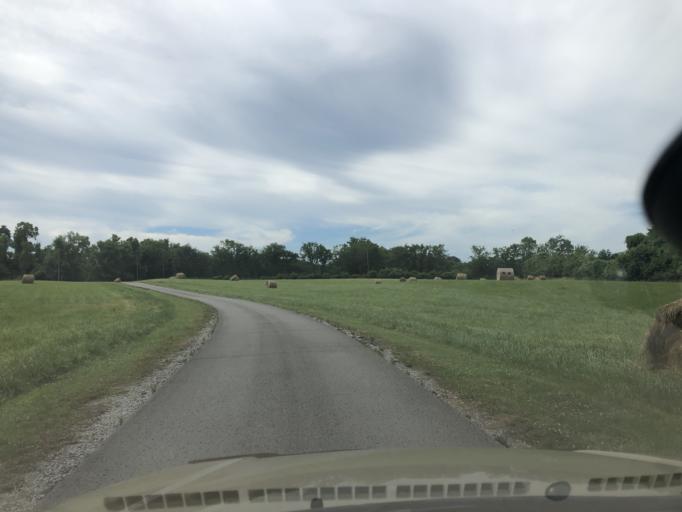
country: US
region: Tennessee
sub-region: Davidson County
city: Lakewood
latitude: 36.2154
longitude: -86.6436
